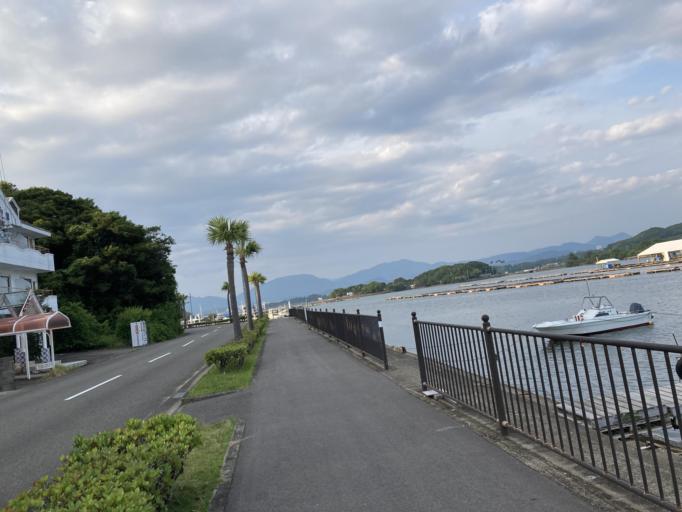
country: JP
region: Wakayama
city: Tanabe
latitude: 33.6825
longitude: 135.3603
